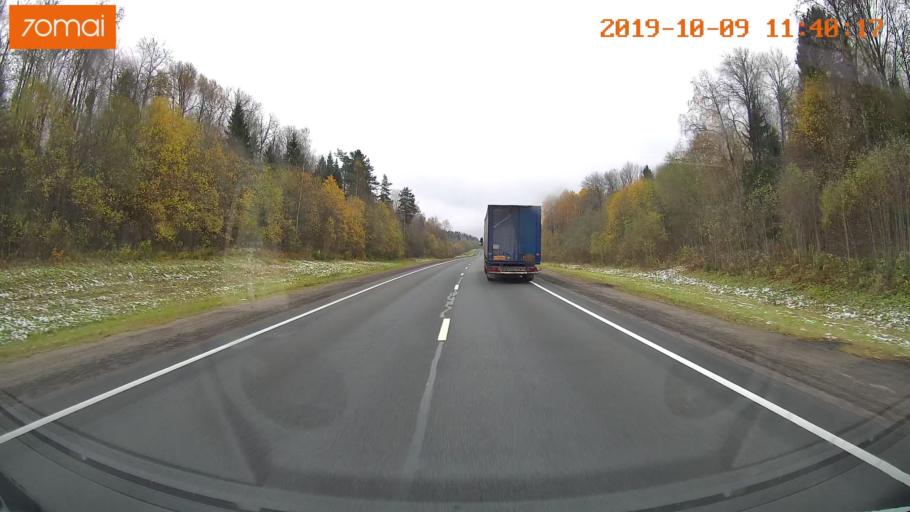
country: RU
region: Vologda
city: Gryazovets
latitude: 58.9445
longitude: 40.1735
